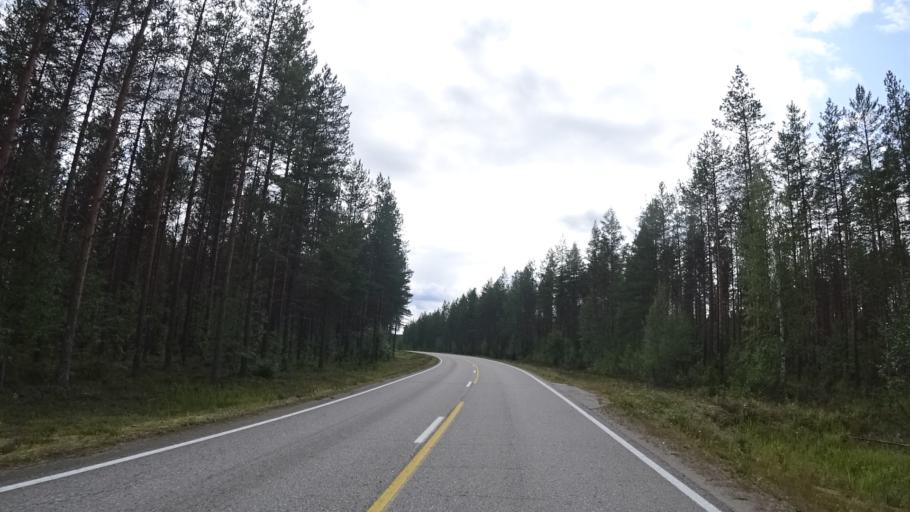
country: FI
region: North Karelia
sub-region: Joensuu
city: Ilomantsi
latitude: 62.7855
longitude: 31.0872
